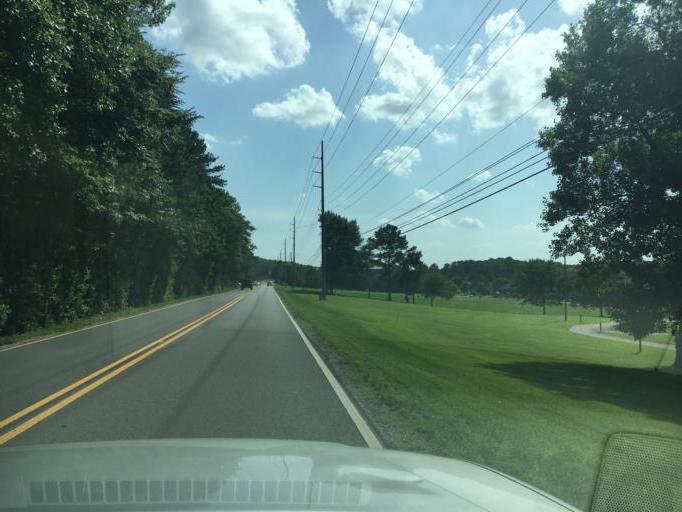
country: US
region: Alabama
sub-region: Shelby County
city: Meadowbrook
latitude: 33.3902
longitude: -86.7230
